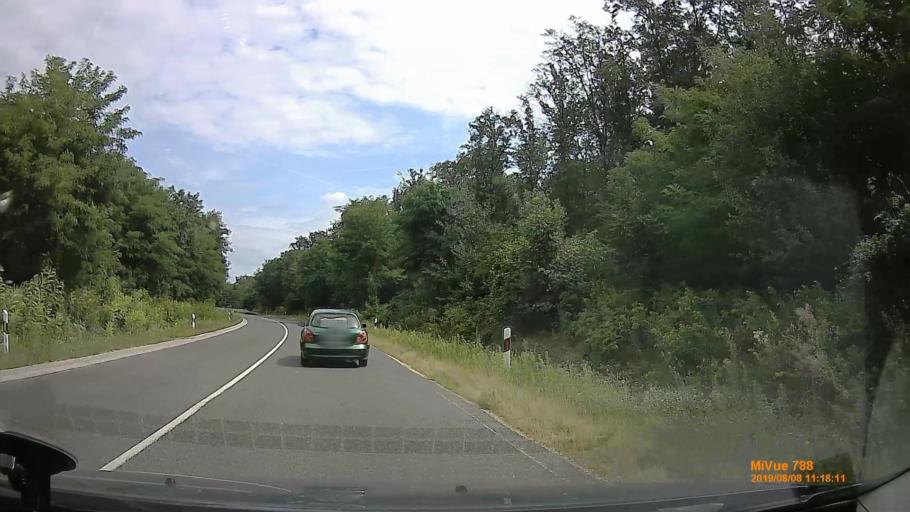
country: HU
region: Somogy
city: Balatonbereny
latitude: 46.6633
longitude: 17.3250
